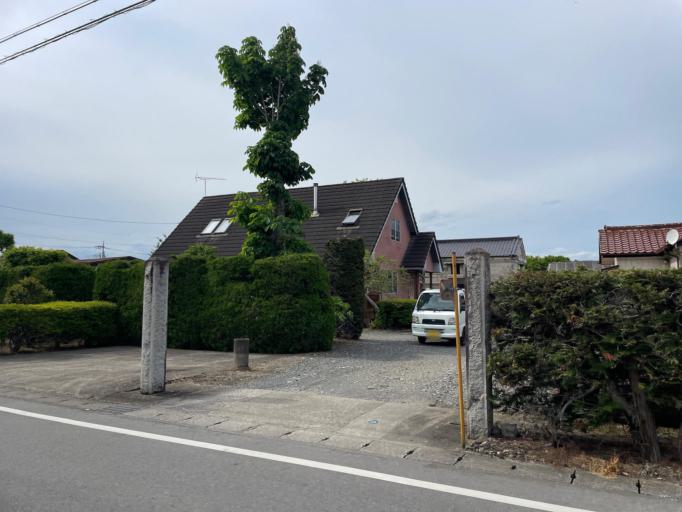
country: JP
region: Tochigi
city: Kanuma
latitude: 36.5067
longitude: 139.7507
